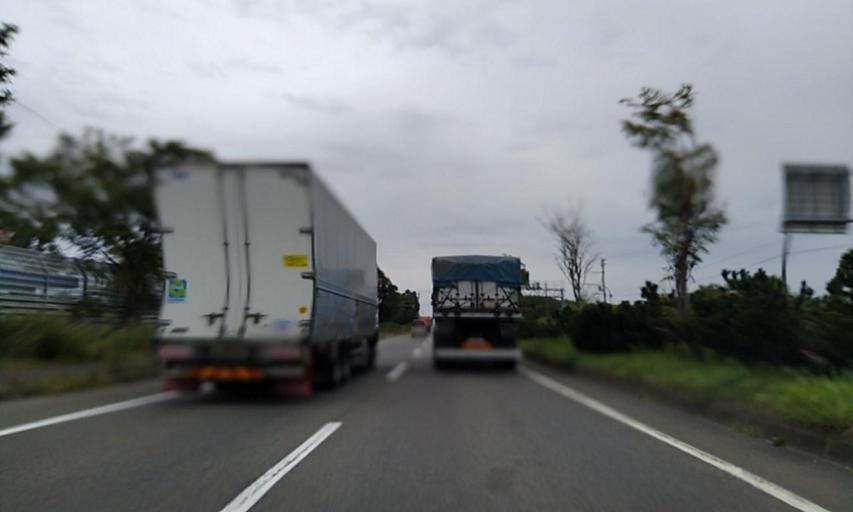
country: JP
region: Hokkaido
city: Ishikari
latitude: 43.1604
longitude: 141.2533
